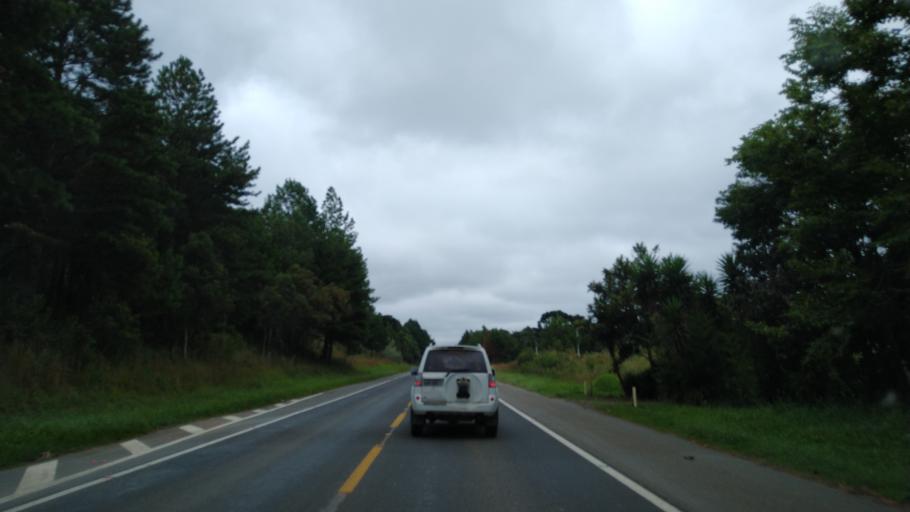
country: BR
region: Santa Catarina
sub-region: Tres Barras
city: Tres Barras
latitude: -26.1799
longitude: -50.1929
